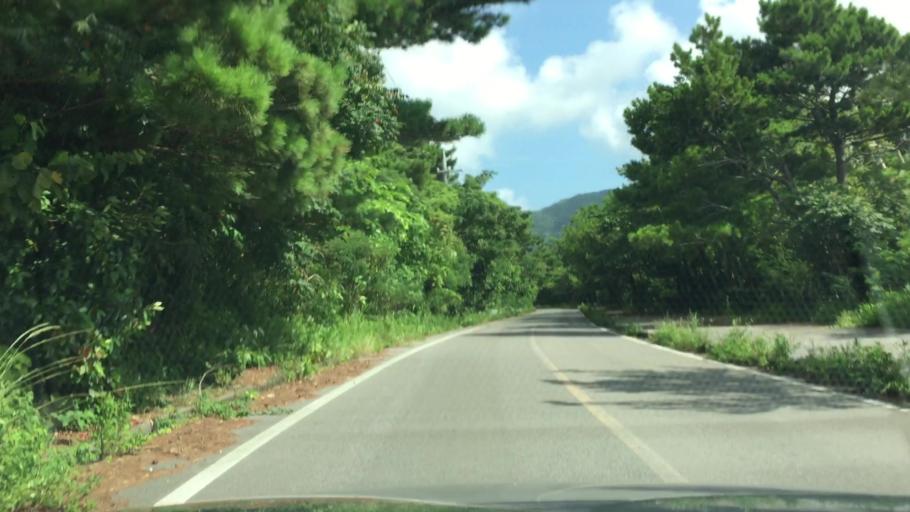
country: JP
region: Okinawa
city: Ishigaki
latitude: 24.4210
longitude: 124.2140
